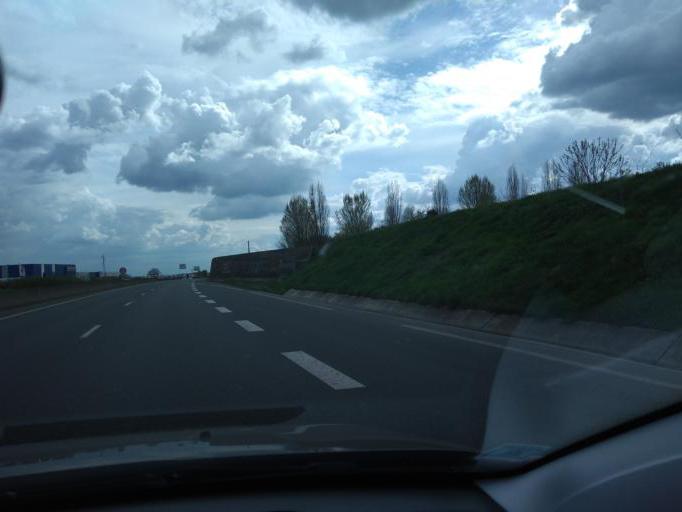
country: FR
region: Pays de la Loire
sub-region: Departement de Maine-et-Loire
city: Avrille
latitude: 47.5082
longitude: -0.6180
